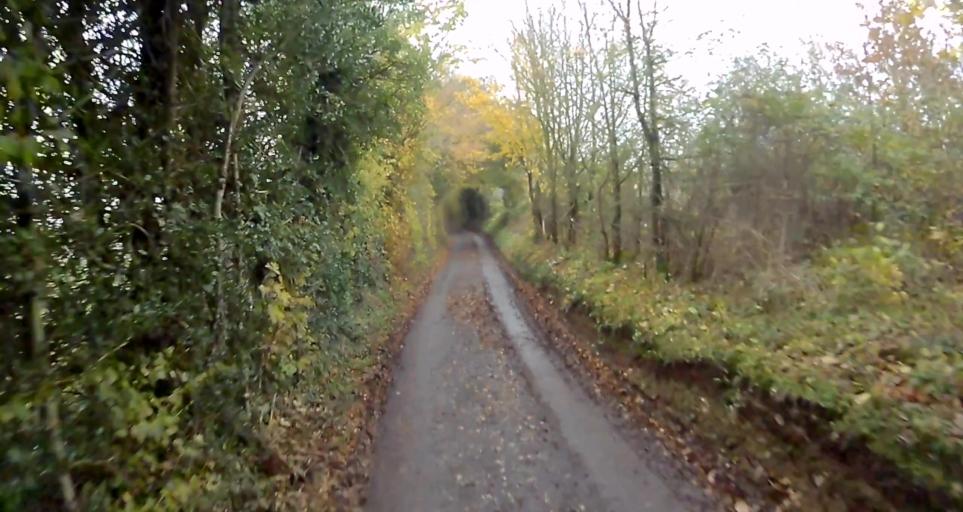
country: GB
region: England
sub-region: Hampshire
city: Odiham
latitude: 51.2416
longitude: -0.9092
